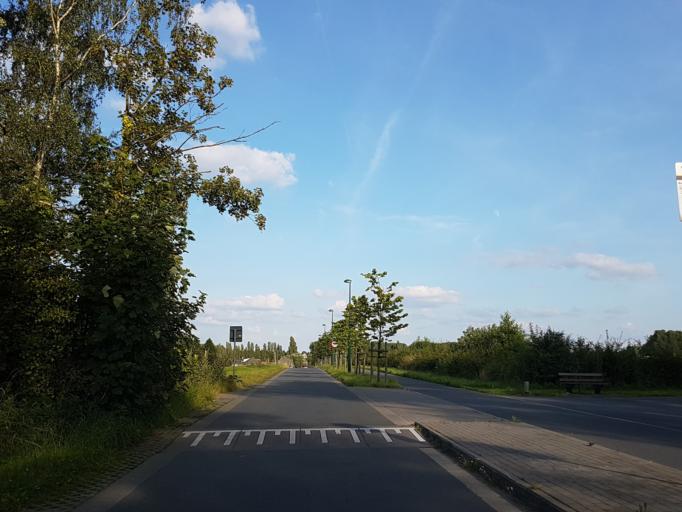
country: BE
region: Flanders
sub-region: Provincie Oost-Vlaanderen
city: Denderleeuw
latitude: 50.9320
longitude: 4.0973
